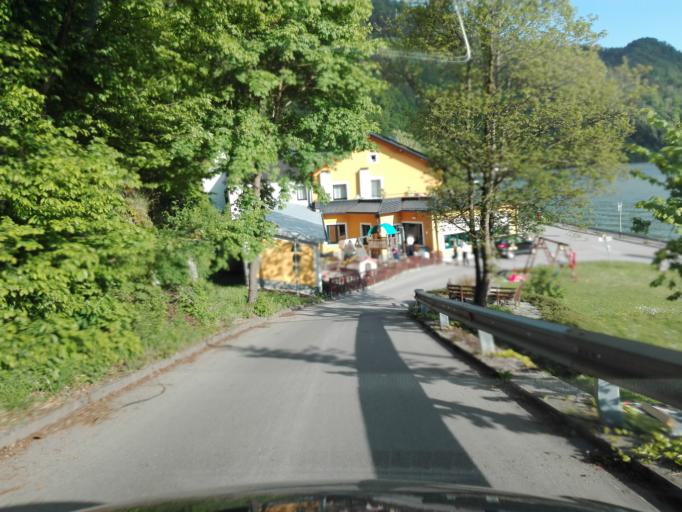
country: AT
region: Upper Austria
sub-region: Politischer Bezirk Rohrbach
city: Atzesberg
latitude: 48.4510
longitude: 13.9180
